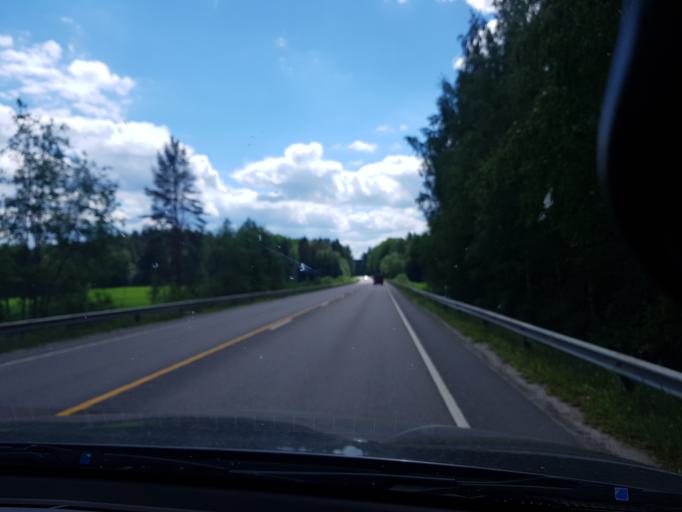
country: FI
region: Haeme
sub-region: Haemeenlinna
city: Parola
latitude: 61.0808
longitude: 24.3952
